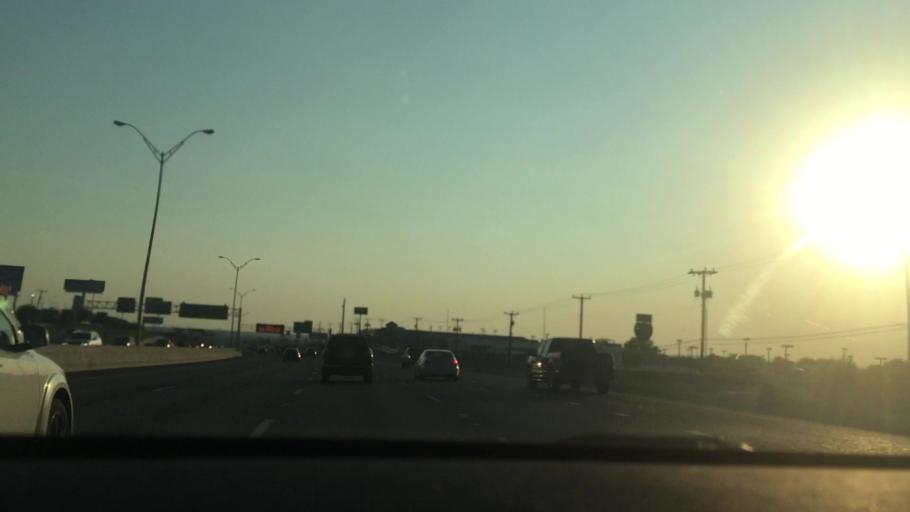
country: US
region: Texas
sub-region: Bexar County
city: Live Oak
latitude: 29.5509
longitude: -98.3597
